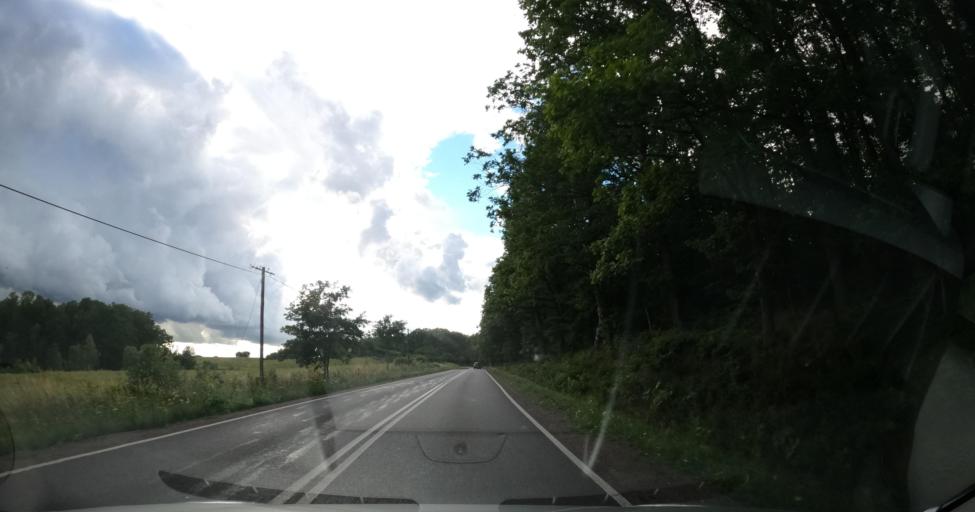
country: PL
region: Pomeranian Voivodeship
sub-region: Powiat bytowski
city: Czarna Dabrowka
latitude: 54.3441
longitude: 17.5950
